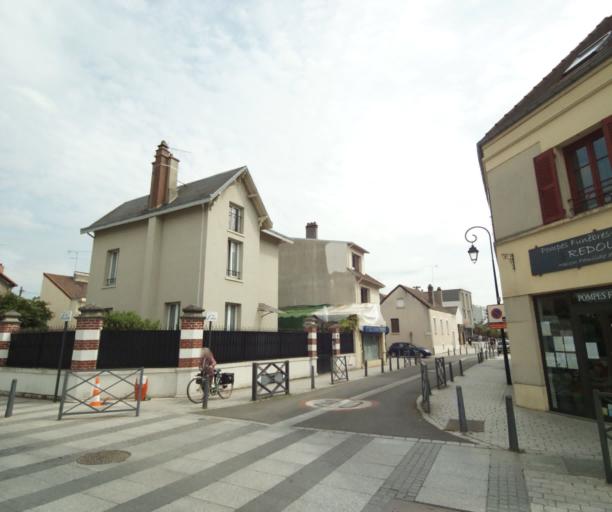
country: FR
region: Ile-de-France
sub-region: Departement des Yvelines
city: Les Mureaux
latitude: 48.9927
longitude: 1.9081
